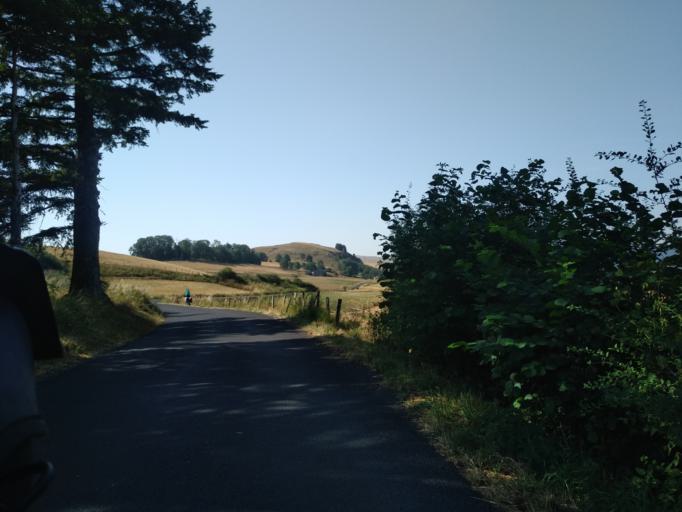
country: FR
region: Auvergne
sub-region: Departement du Cantal
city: Riom-es-Montagnes
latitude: 45.2539
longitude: 2.7435
